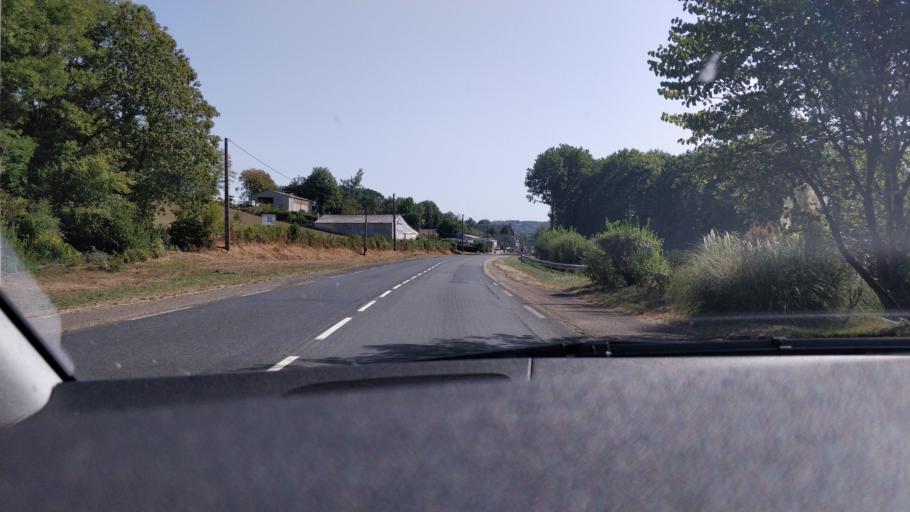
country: FR
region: Limousin
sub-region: Departement de la Correze
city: Uzerche
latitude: 45.4494
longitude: 1.5598
